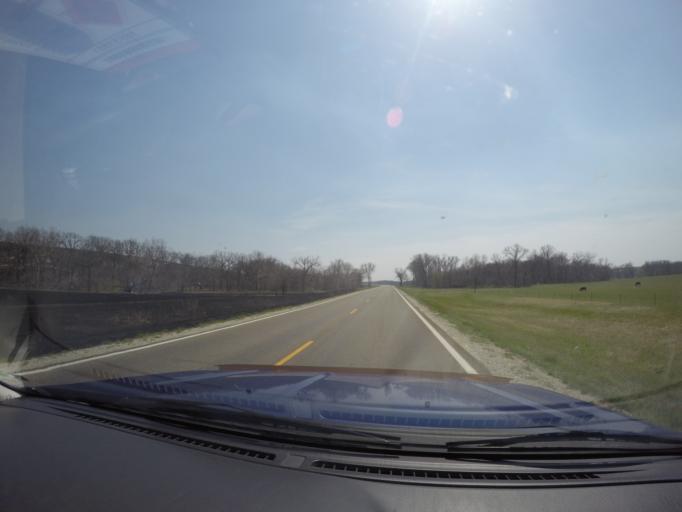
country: US
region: Kansas
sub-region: Chase County
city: Cottonwood Falls
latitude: 38.4817
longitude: -96.5573
